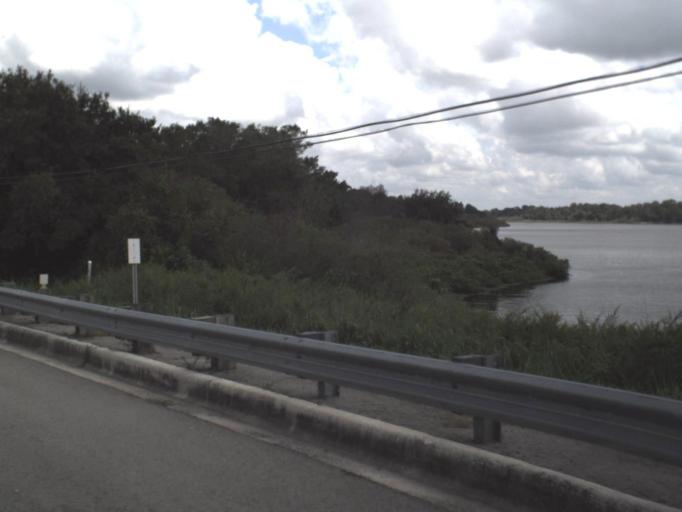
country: US
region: Florida
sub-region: Sarasota County
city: The Meadows
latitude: 27.4758
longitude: -82.3010
